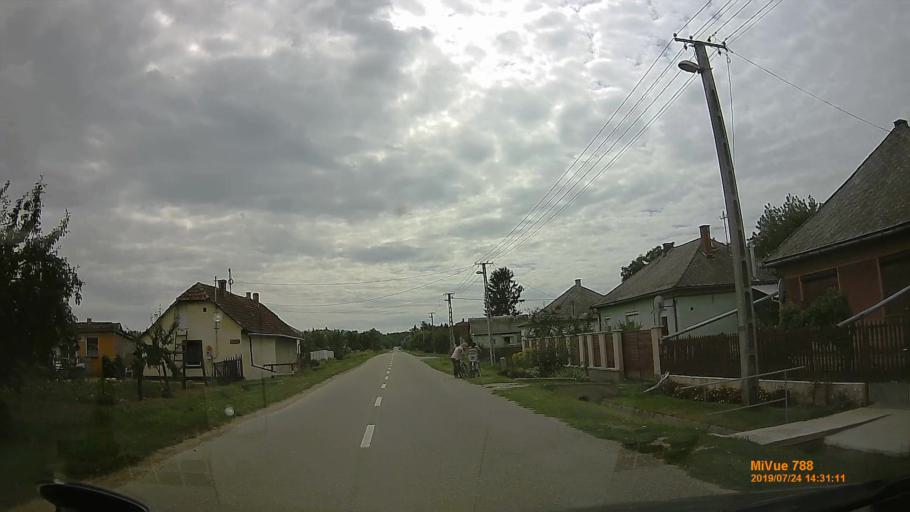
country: HU
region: Szabolcs-Szatmar-Bereg
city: Mandok
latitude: 48.3217
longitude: 22.2637
